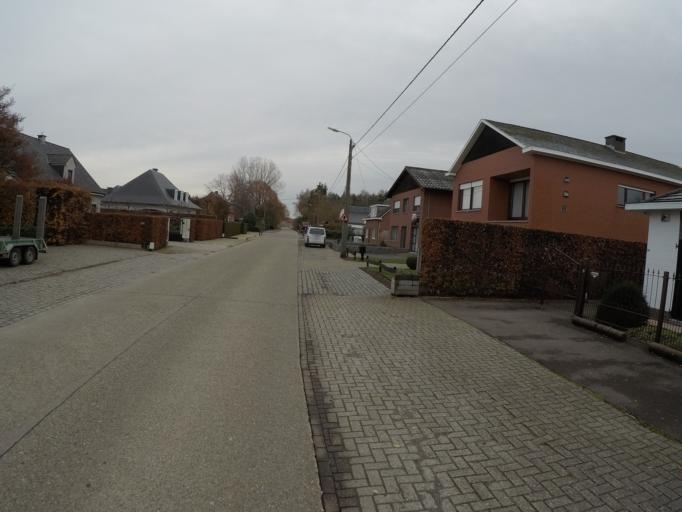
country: BE
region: Flanders
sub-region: Provincie Antwerpen
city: Heist-op-den-Berg
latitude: 51.1002
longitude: 4.7189
